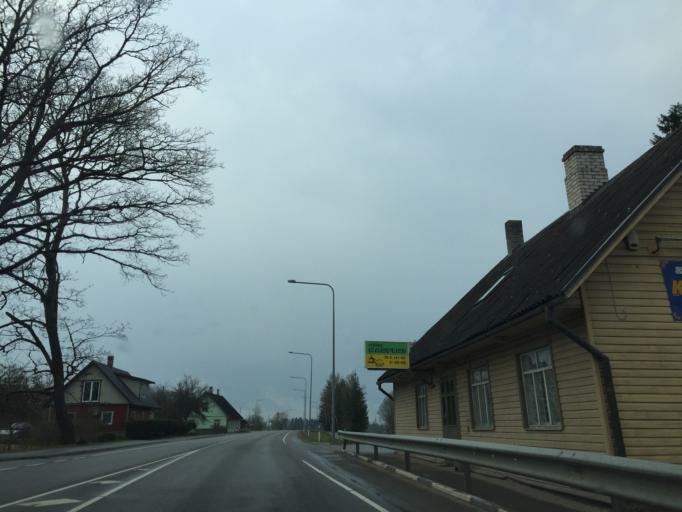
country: EE
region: Tartu
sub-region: UElenurme vald
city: Ulenurme
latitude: 58.1452
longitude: 26.7021
